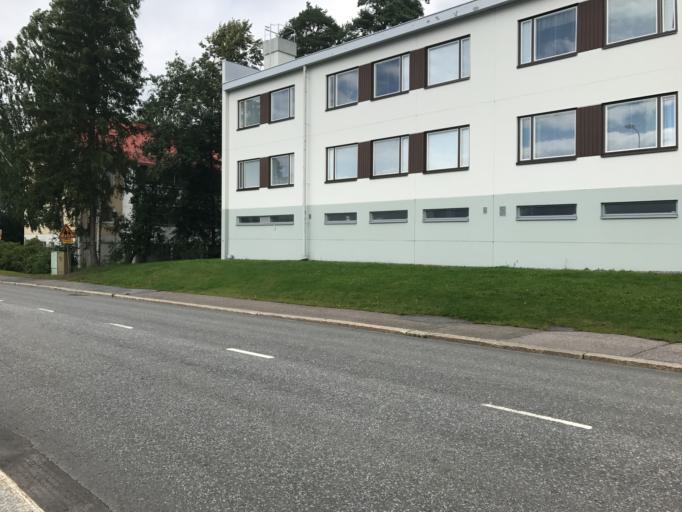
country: FI
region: Pirkanmaa
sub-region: Etelae-Pirkanmaa
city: Valkeakoski
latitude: 61.2625
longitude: 24.0393
